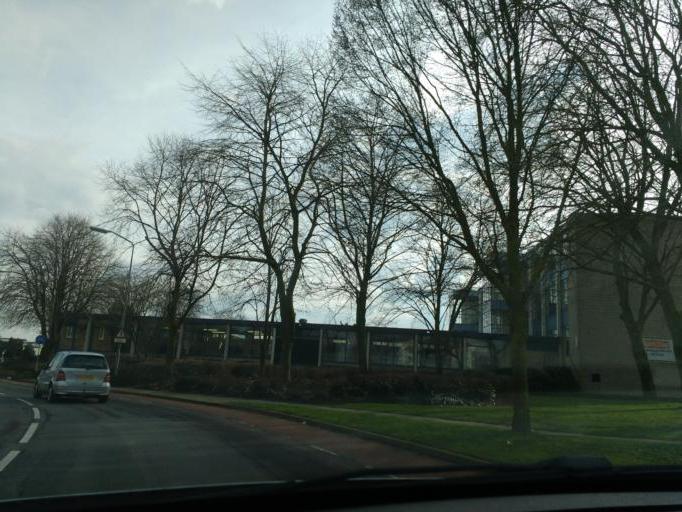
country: NL
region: North Brabant
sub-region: Gemeente Boxmeer
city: Boxmeer
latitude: 51.6456
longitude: 5.9474
